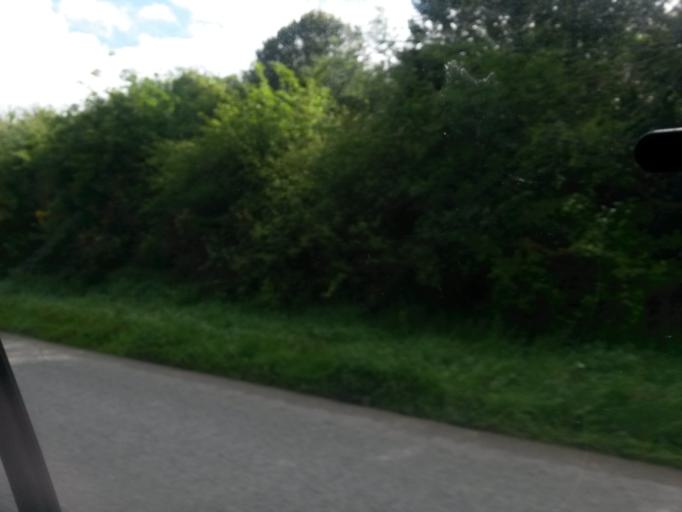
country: IE
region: Leinster
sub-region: Loch Garman
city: Enniscorthy
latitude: 52.5361
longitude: -6.5535
